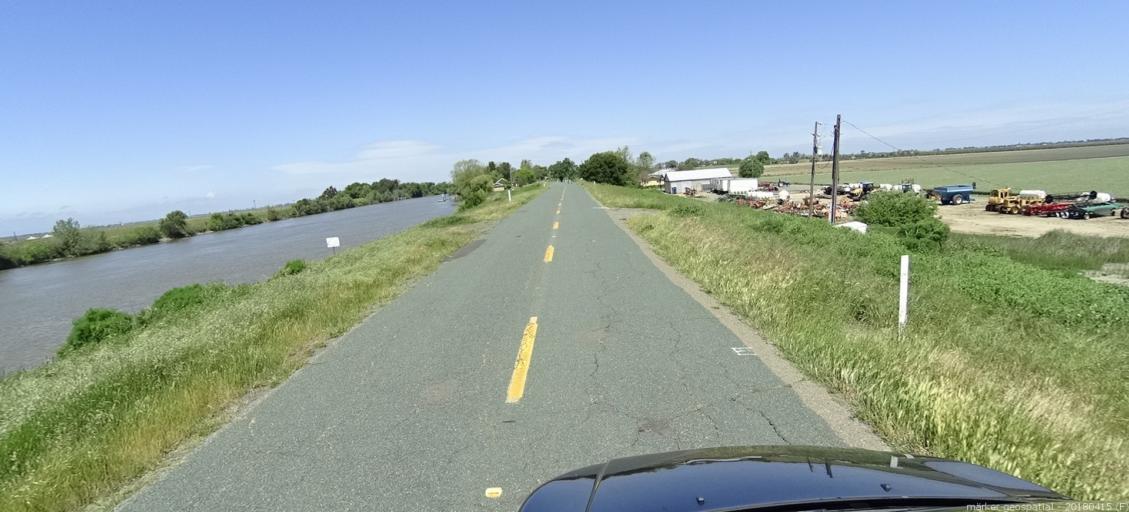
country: US
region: California
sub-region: Sacramento County
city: Walnut Grove
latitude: 38.2455
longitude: -121.6009
